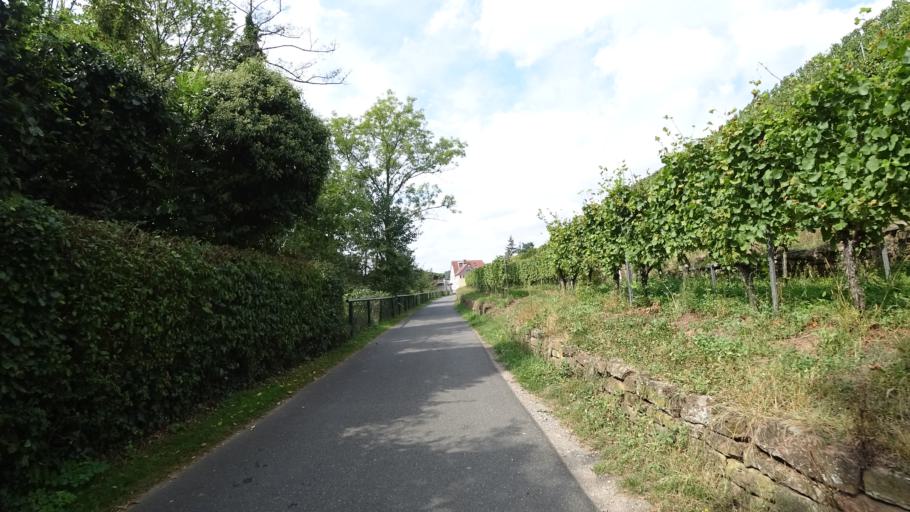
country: DE
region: Bavaria
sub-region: Regierungsbezirk Unterfranken
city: Burgstadt
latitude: 49.7107
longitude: 9.2763
